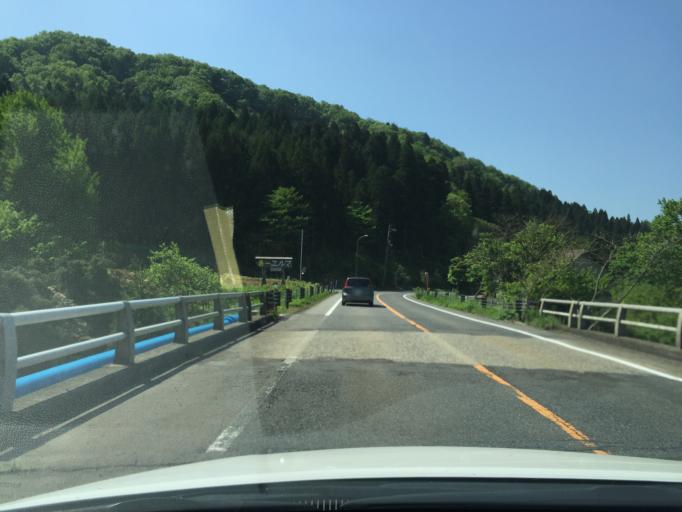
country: JP
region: Niigata
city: Muramatsu
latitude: 37.6538
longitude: 139.1365
